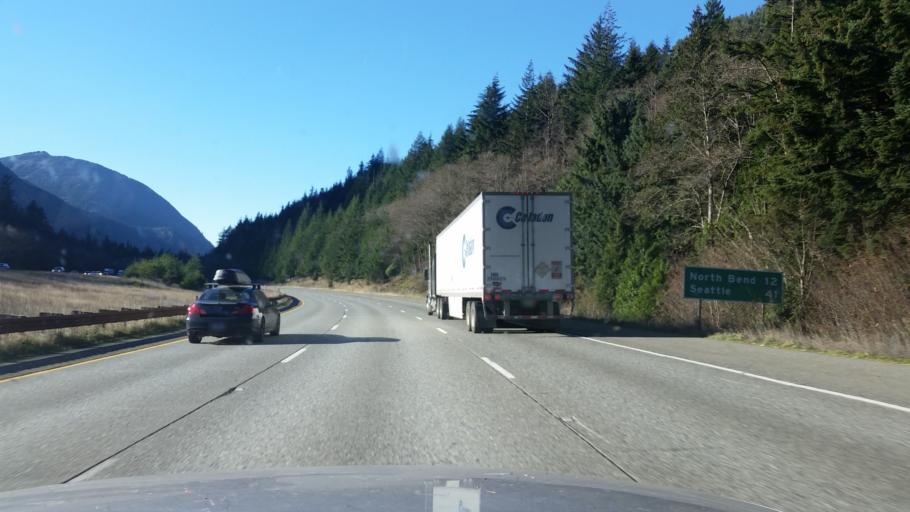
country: US
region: Washington
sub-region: King County
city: Tanner
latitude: 47.4247
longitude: -121.5967
